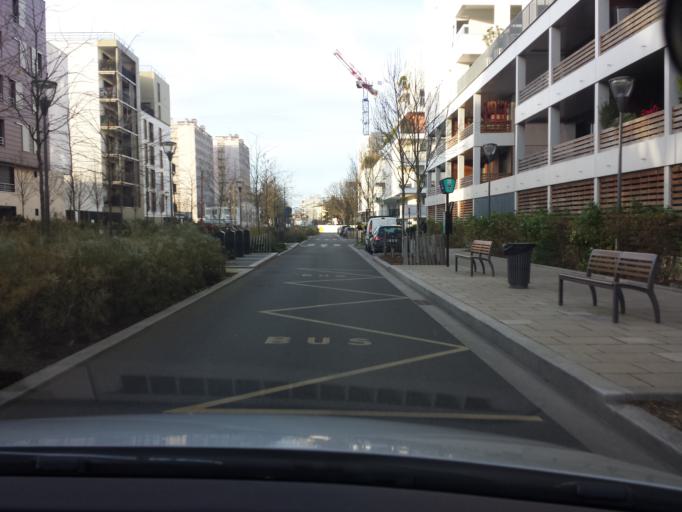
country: FR
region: Ile-de-France
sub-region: Departement de l'Essonne
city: Palaiseau
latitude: 48.7214
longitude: 2.2639
